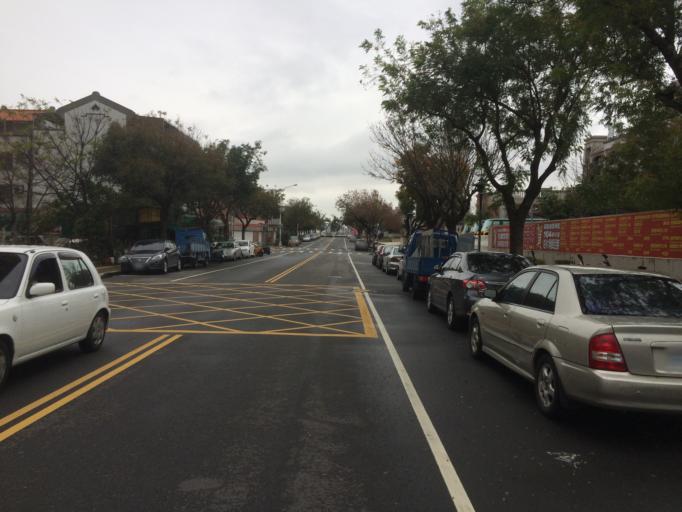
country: TW
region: Taiwan
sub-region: Taichung City
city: Taichung
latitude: 24.1782
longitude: 120.7129
